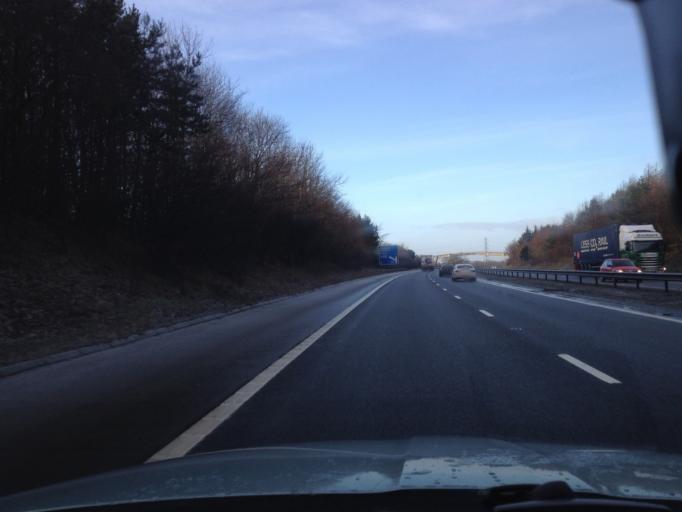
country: GB
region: Scotland
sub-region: West Lothian
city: Blackburn
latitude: 55.8783
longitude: -3.6290
